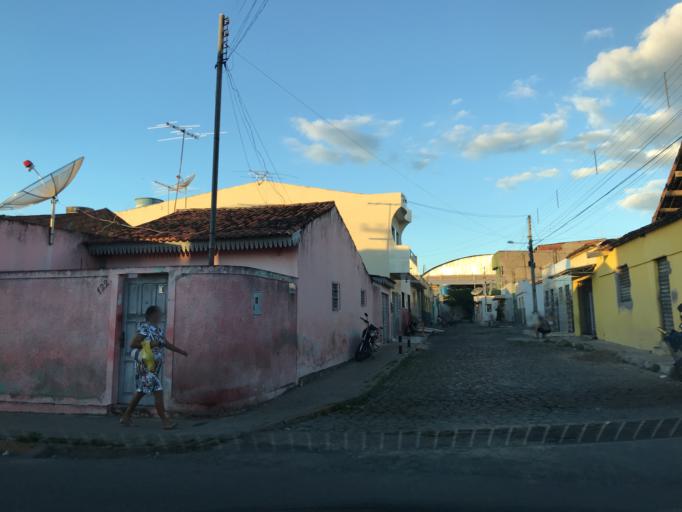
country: BR
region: Pernambuco
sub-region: Bezerros
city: Bezerros
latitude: -8.2377
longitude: -35.7574
